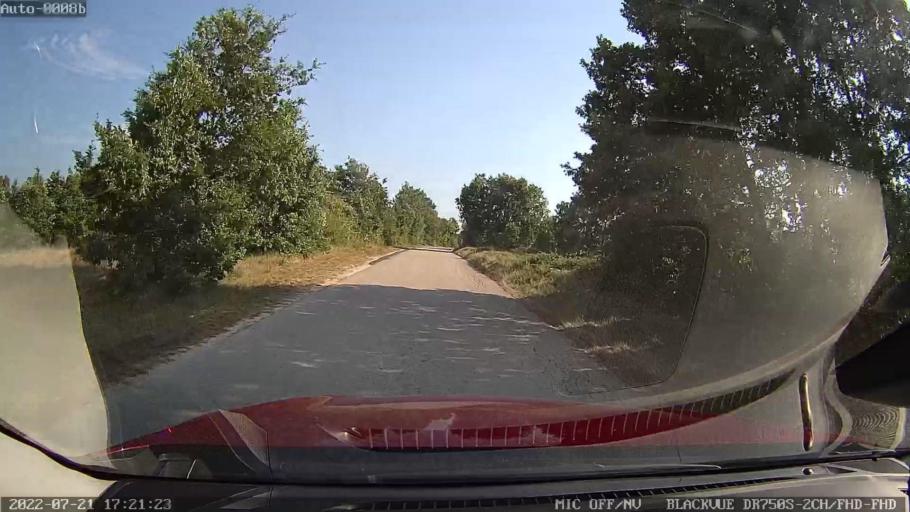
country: HR
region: Istarska
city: Karojba
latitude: 45.1954
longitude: 13.8300
